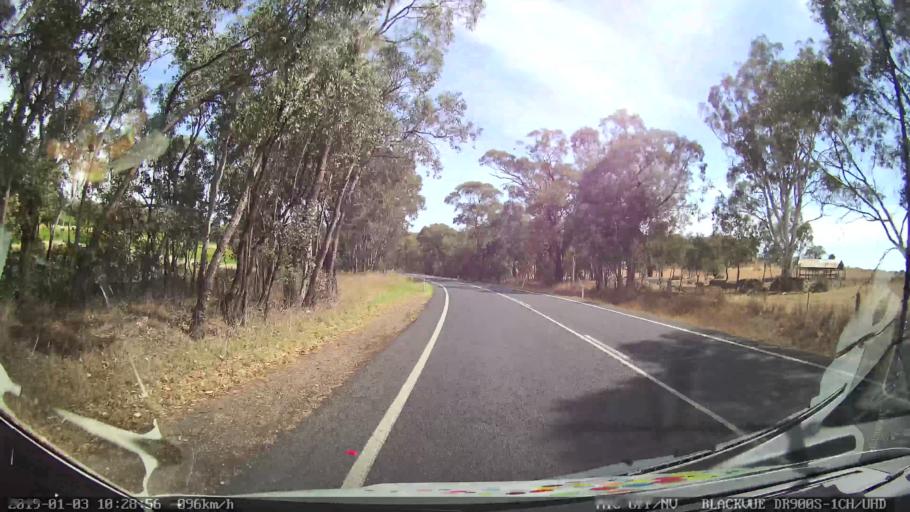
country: AU
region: New South Wales
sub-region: Young
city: Young
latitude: -34.3808
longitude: 148.2601
